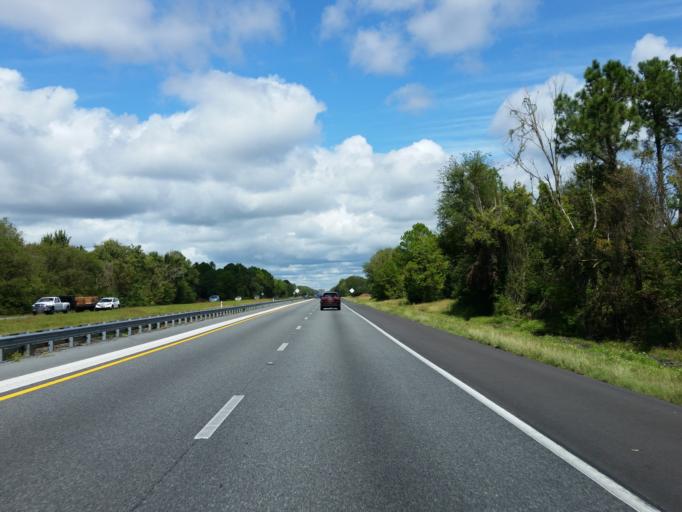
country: US
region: Florida
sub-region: Sumter County
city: Lake Panasoffkee
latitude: 28.8138
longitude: -82.0887
